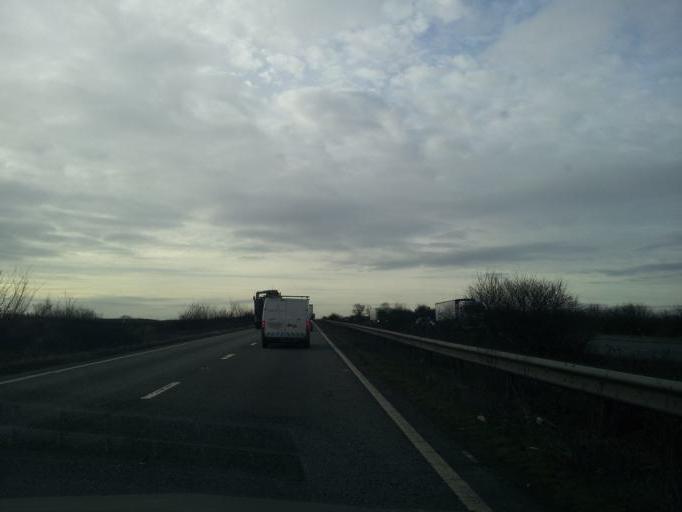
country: GB
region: England
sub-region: District of Rutland
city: Greetham
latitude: 52.7724
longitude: -0.6112
